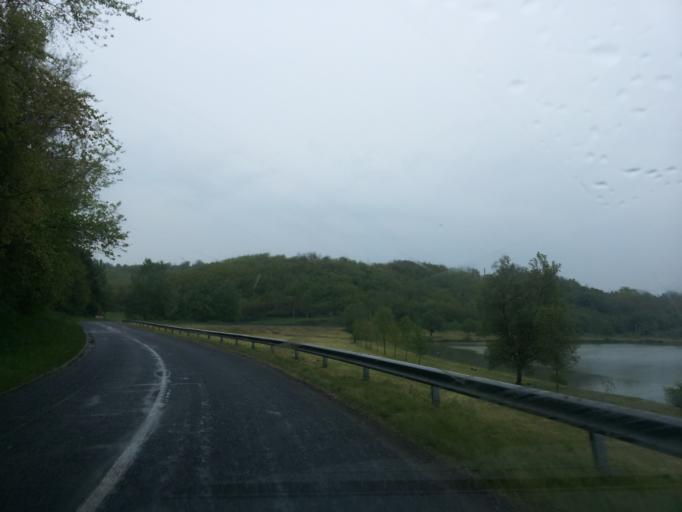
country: HU
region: Tolna
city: Bonyhad
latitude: 46.2713
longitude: 18.6297
